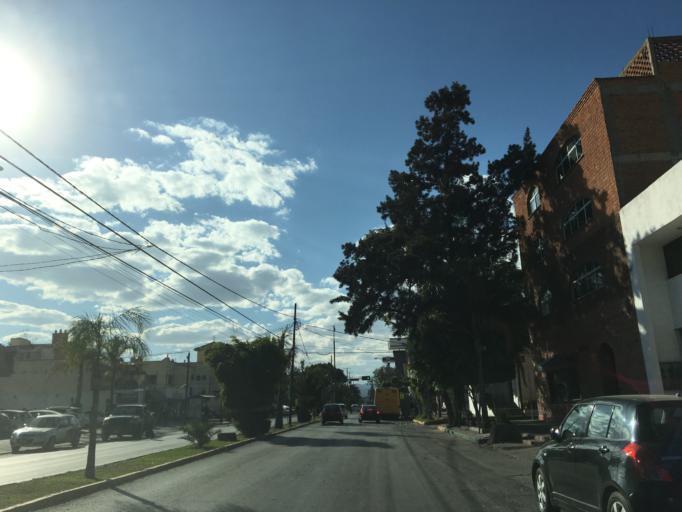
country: MX
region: San Luis Potosi
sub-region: San Luis Potosi
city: San Luis Potosi
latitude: 22.1502
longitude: -100.9935
